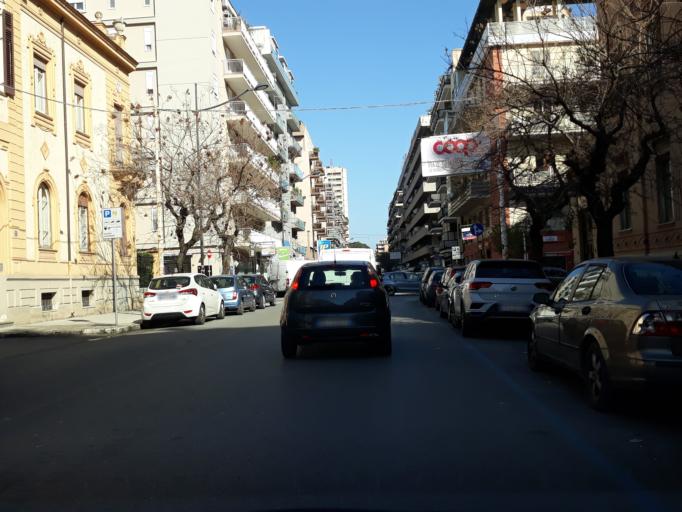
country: IT
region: Sicily
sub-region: Palermo
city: Palermo
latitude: 38.1340
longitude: 13.3460
